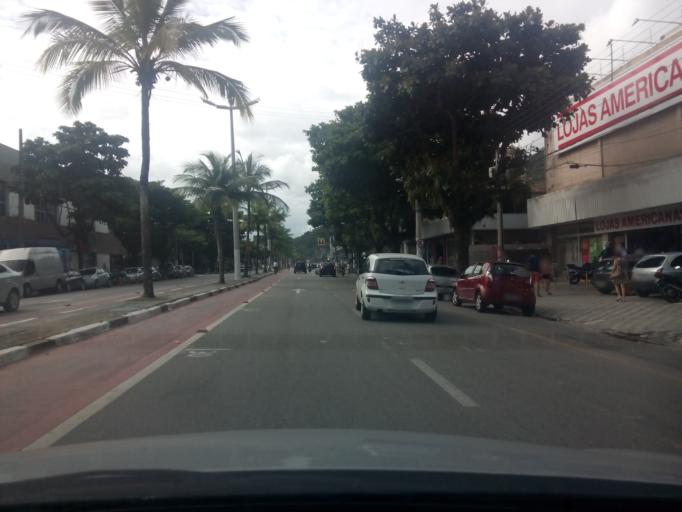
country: BR
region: Sao Paulo
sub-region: Guaruja
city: Guaruja
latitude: -23.9947
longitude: -46.2570
